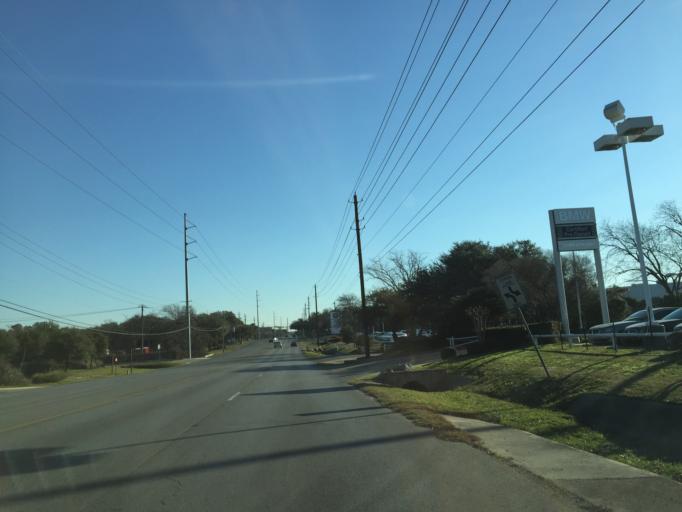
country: US
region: Texas
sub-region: Williamson County
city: Jollyville
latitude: 30.4364
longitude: -97.7634
